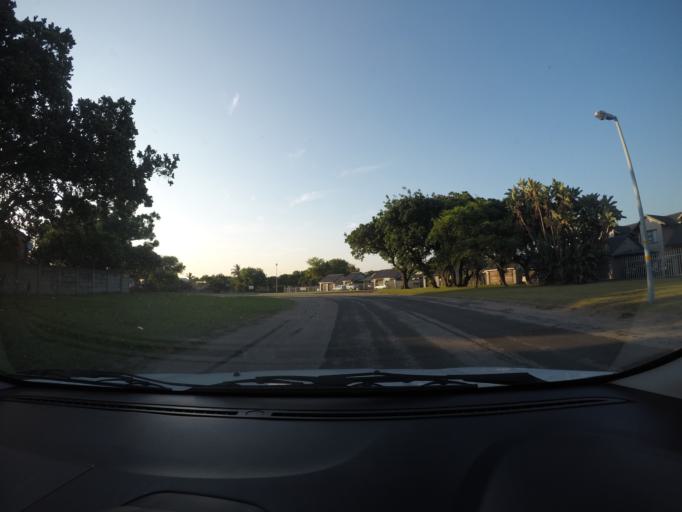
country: ZA
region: KwaZulu-Natal
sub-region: uThungulu District Municipality
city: Richards Bay
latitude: -28.7804
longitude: 32.1018
